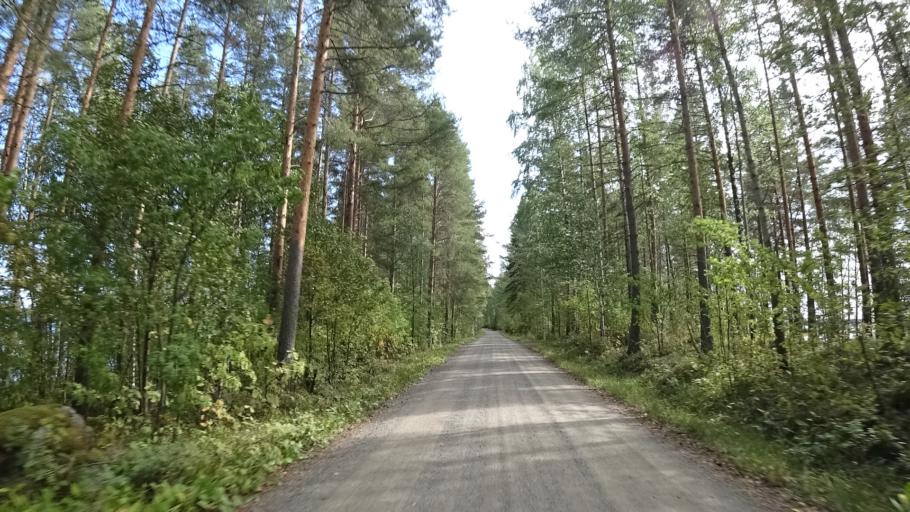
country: FI
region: North Karelia
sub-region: Joensuu
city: Pyhaeselkae
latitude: 62.3881
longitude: 29.7883
